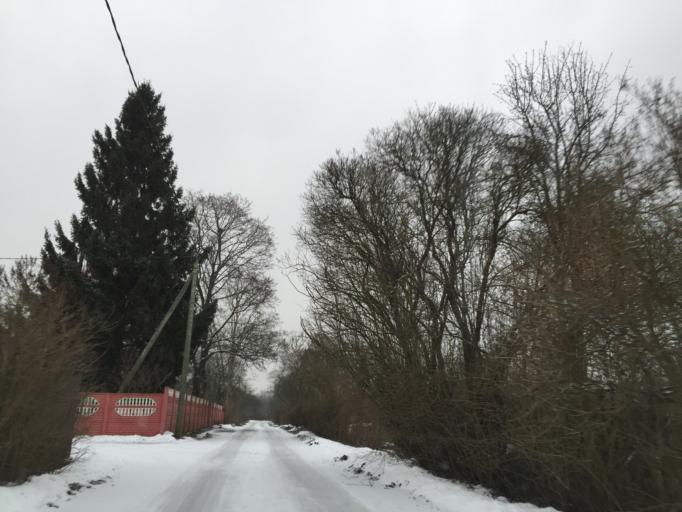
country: LV
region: Riga
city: Riga
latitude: 56.9227
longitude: 24.1280
